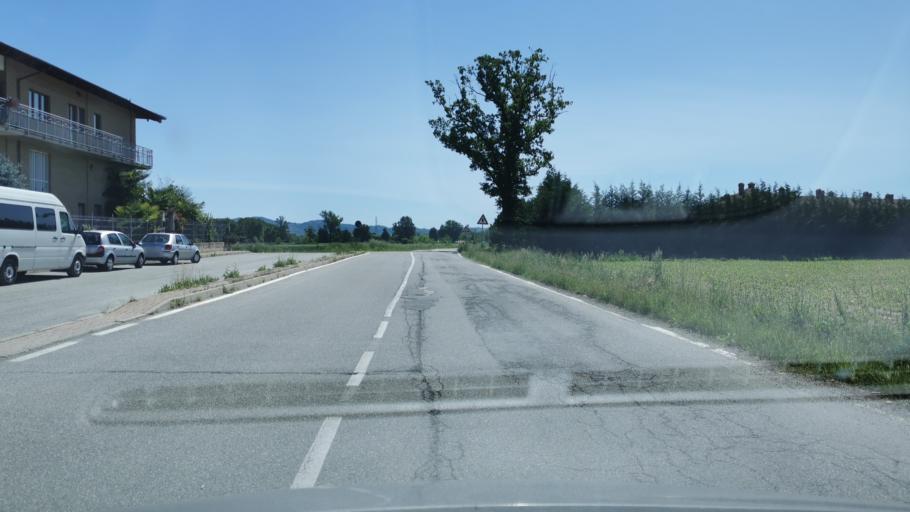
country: IT
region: Piedmont
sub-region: Provincia di Torino
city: Leini
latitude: 45.1732
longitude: 7.7260
